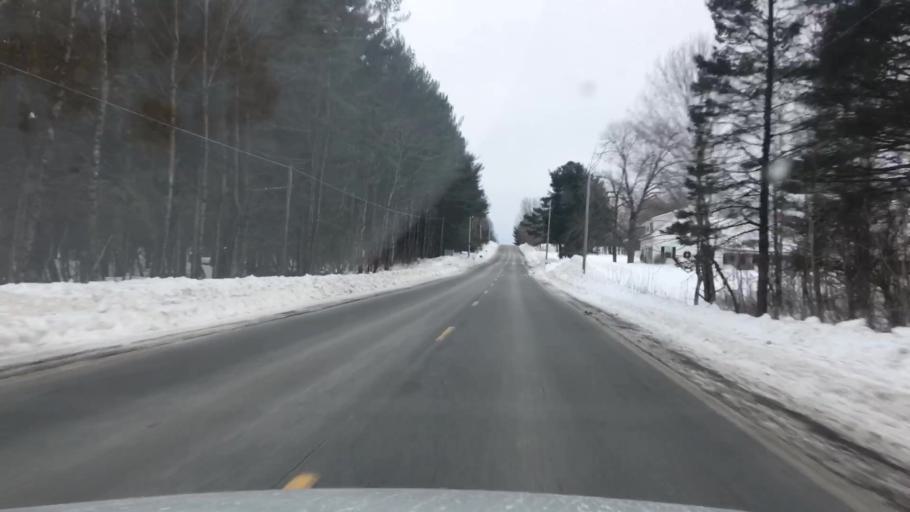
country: US
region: Maine
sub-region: Penobscot County
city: Garland
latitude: 44.9636
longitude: -69.1893
